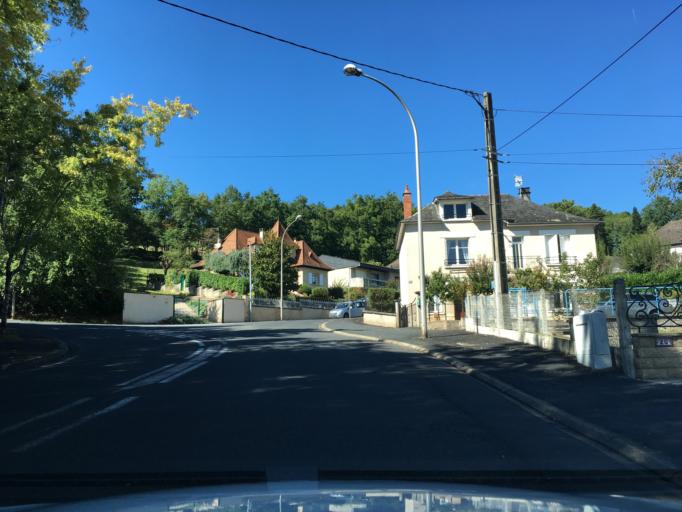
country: FR
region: Limousin
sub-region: Departement de la Correze
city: Ussac
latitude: 45.1704
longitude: 1.5093
